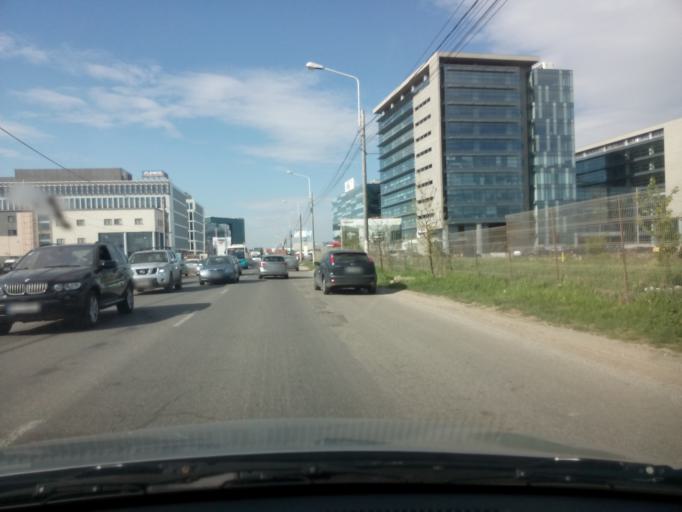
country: RO
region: Ilfov
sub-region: Voluntari City
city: Voluntari
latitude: 44.4874
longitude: 26.1263
